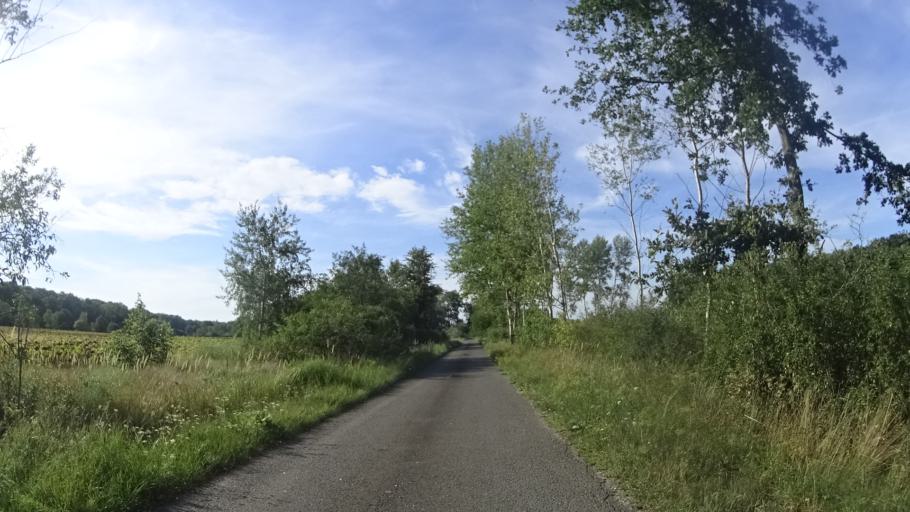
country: AT
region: Lower Austria
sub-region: Politischer Bezirk Ganserndorf
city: Drosing
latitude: 48.5644
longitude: 16.9563
